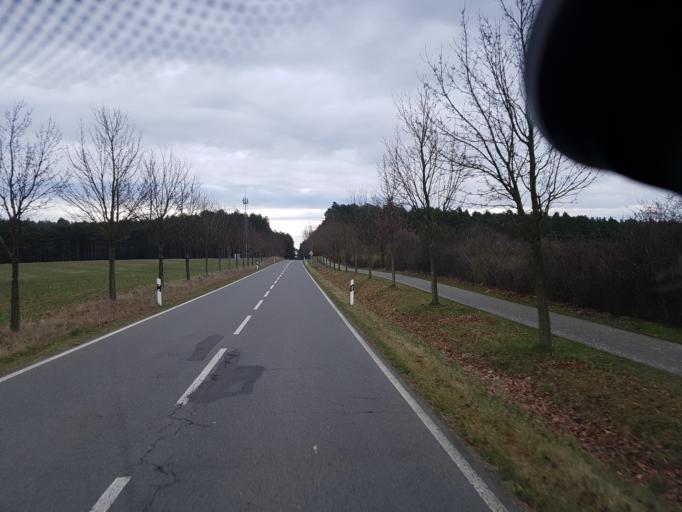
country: DE
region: Brandenburg
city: Mixdorf
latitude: 52.1930
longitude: 14.4156
